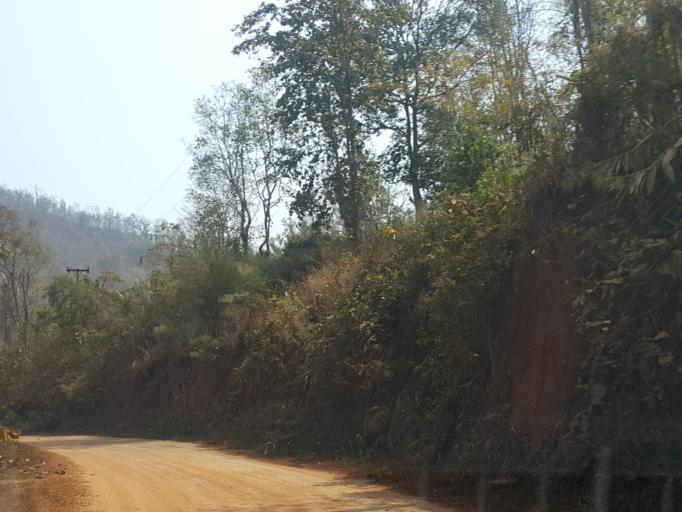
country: TH
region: Chiang Mai
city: Hang Dong
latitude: 18.7465
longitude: 98.8257
